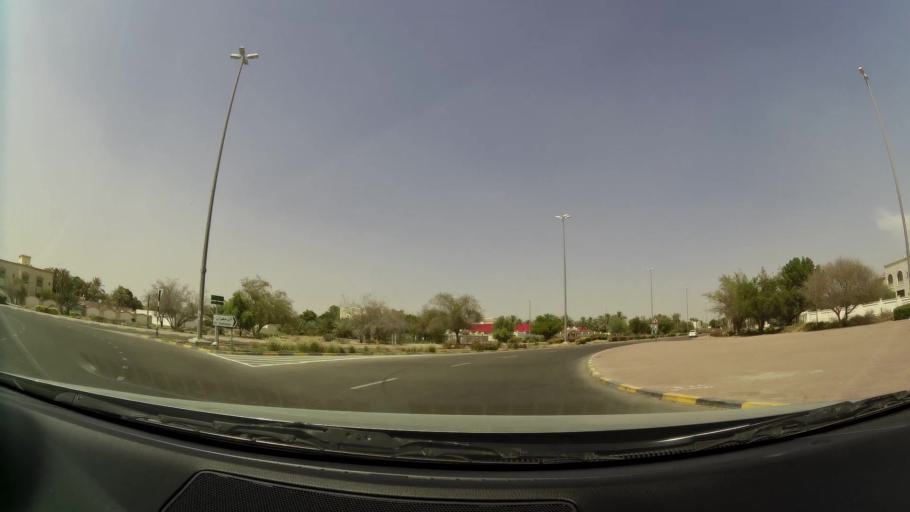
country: AE
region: Abu Dhabi
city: Al Ain
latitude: 24.2332
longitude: 55.7072
